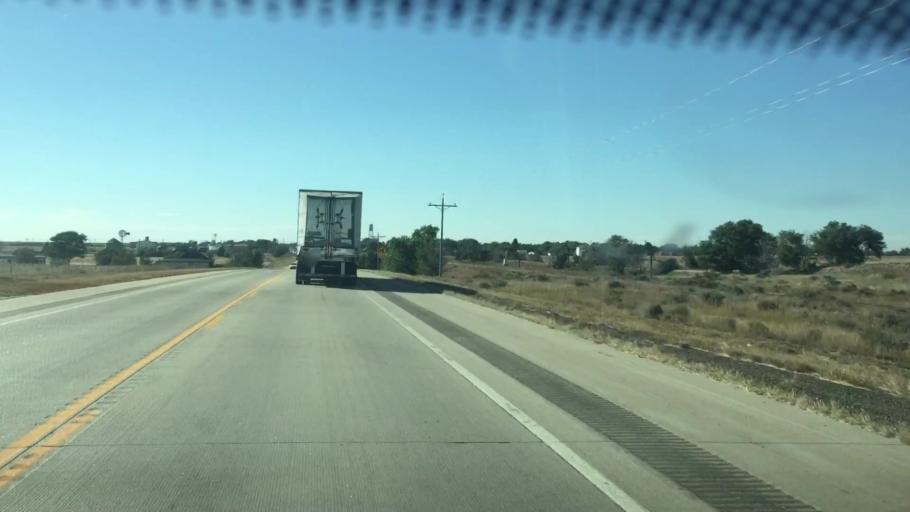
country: US
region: Colorado
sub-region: Kiowa County
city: Eads
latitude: 38.4765
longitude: -102.7646
